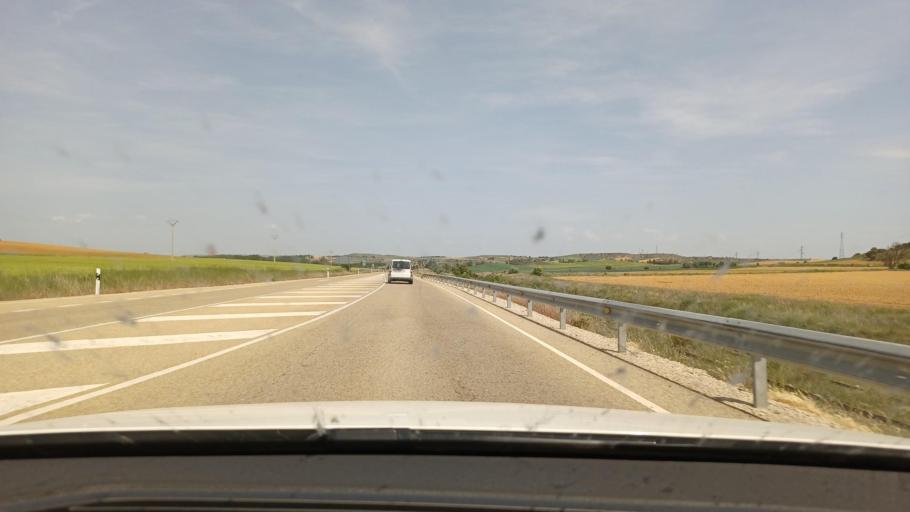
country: ES
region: Castille and Leon
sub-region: Provincia de Soria
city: Barca
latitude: 41.4651
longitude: -2.6321
